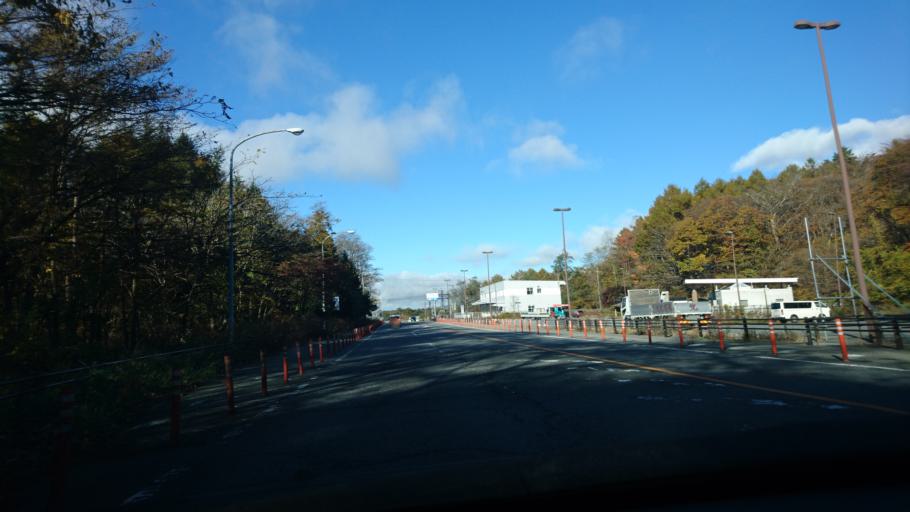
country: JP
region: Nagano
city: Saku
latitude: 36.3272
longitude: 138.6423
